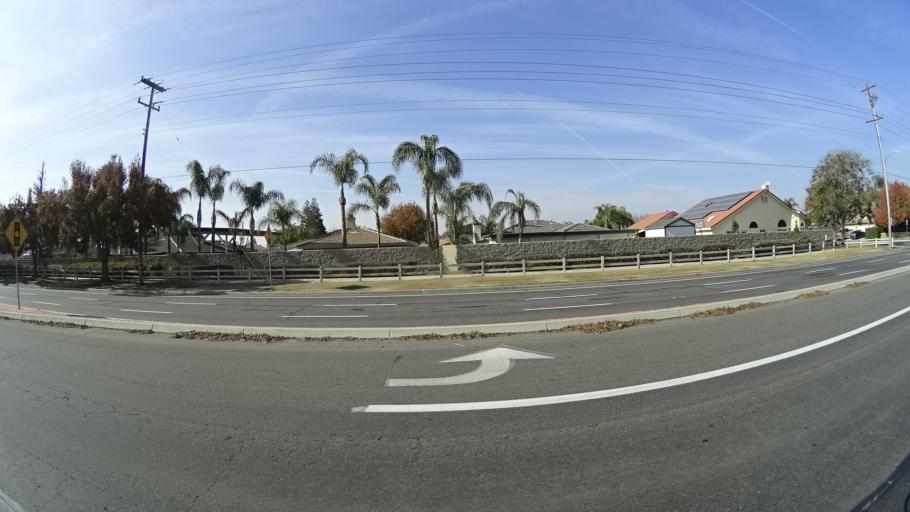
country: US
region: California
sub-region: Kern County
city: Greenacres
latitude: 35.4072
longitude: -119.1099
